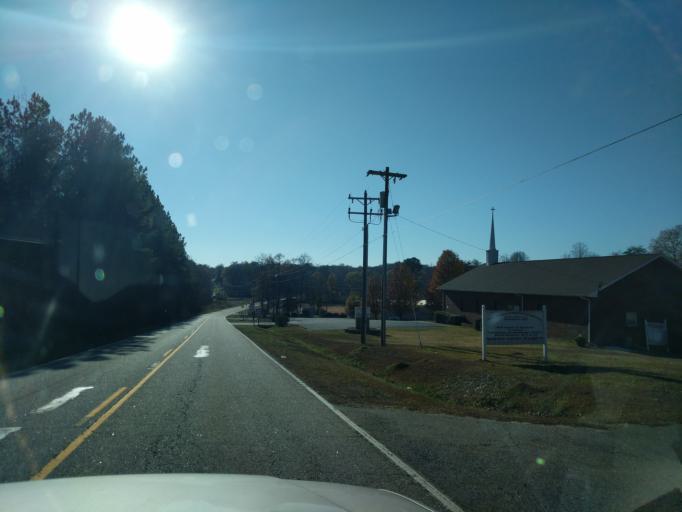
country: US
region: South Carolina
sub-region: Spartanburg County
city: Landrum
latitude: 35.1232
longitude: -82.1403
